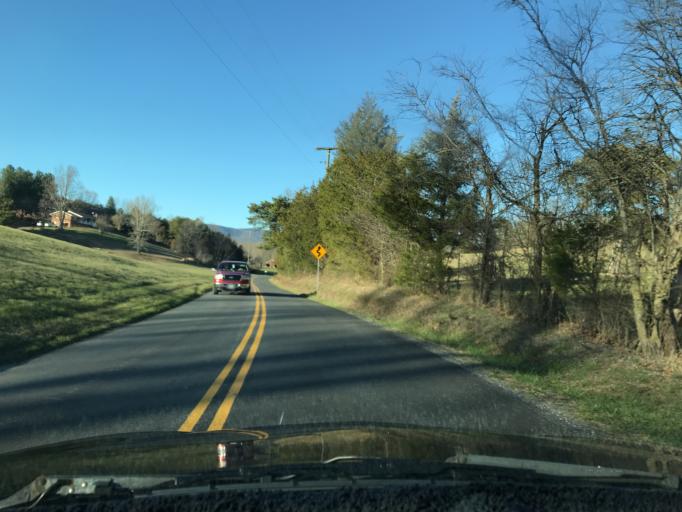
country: US
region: Virginia
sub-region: Botetourt County
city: Blue Ridge
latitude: 37.4114
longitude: -79.7031
